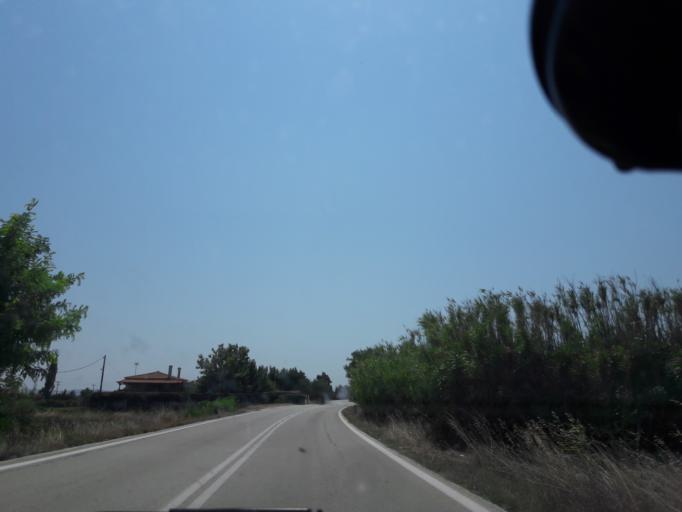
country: GR
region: North Aegean
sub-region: Nomos Lesvou
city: Myrina
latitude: 39.9322
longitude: 25.3407
